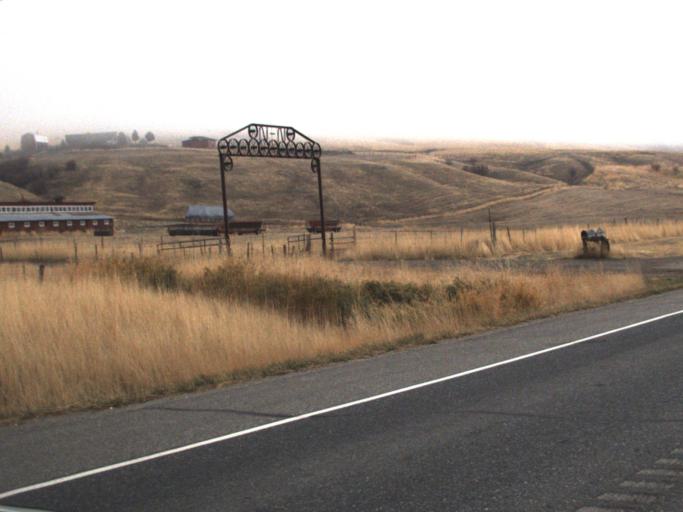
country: US
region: Washington
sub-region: Stevens County
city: Kettle Falls
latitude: 48.6043
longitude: -118.0239
